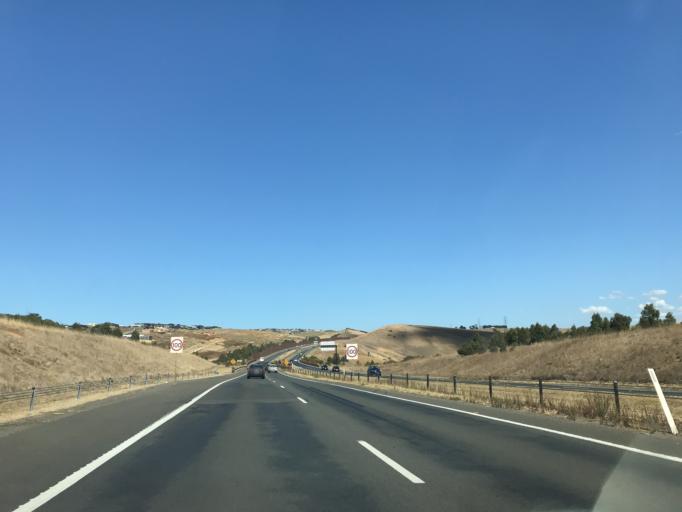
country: AU
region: Victoria
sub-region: Greater Geelong
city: Wandana Heights
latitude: -38.1486
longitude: 144.2953
